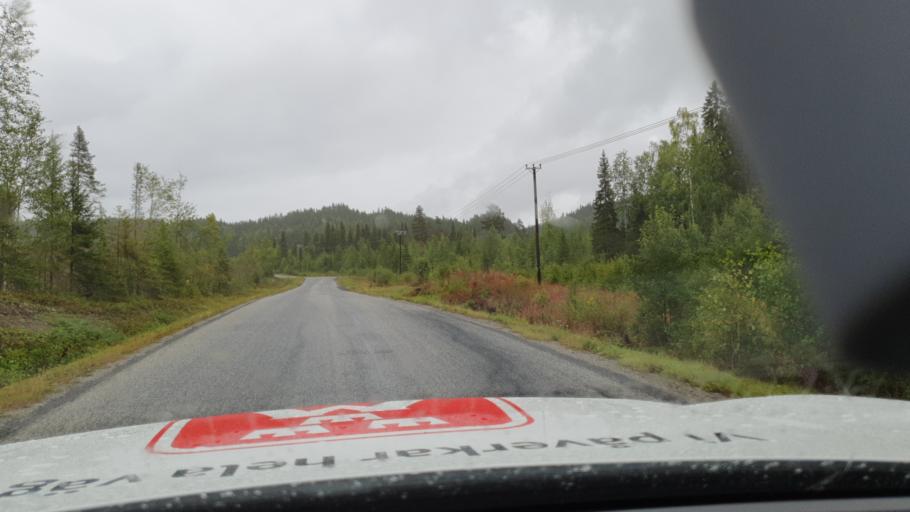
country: SE
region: Vaesterbotten
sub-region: Dorotea Kommun
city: Dorotea
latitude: 64.1270
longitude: 16.2704
